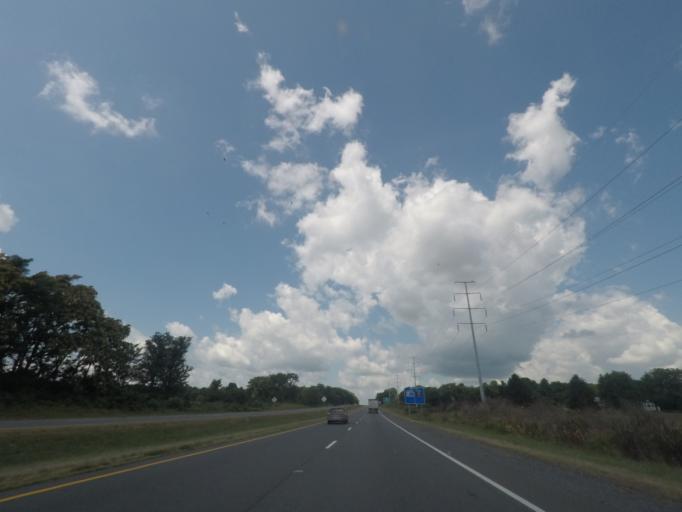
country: US
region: Virginia
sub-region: City of Winchester
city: Winchester
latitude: 39.2131
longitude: -78.1545
